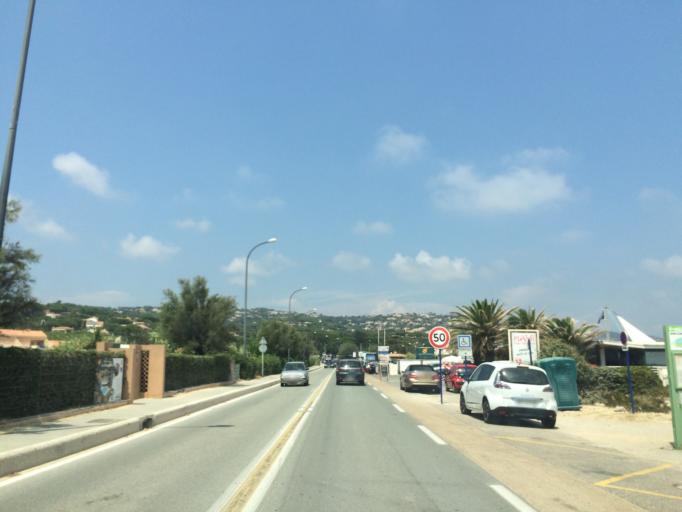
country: FR
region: Provence-Alpes-Cote d'Azur
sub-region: Departement du Var
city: Sainte-Maxime
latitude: 43.3208
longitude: 6.6646
